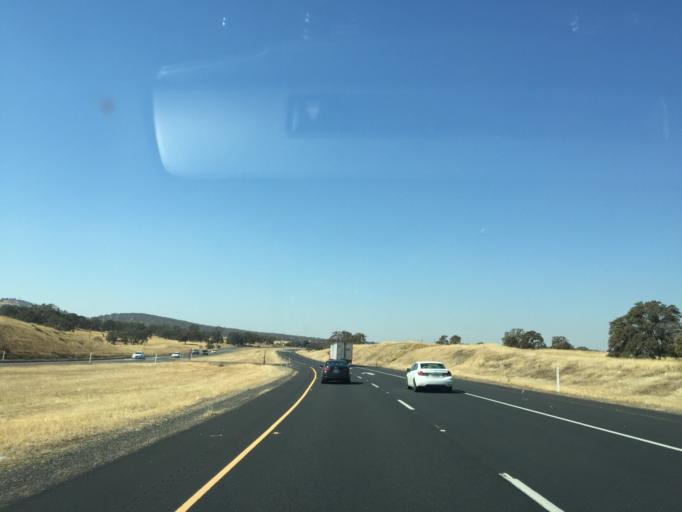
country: US
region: California
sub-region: Tuolumne County
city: Jamestown
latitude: 37.8438
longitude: -120.5336
